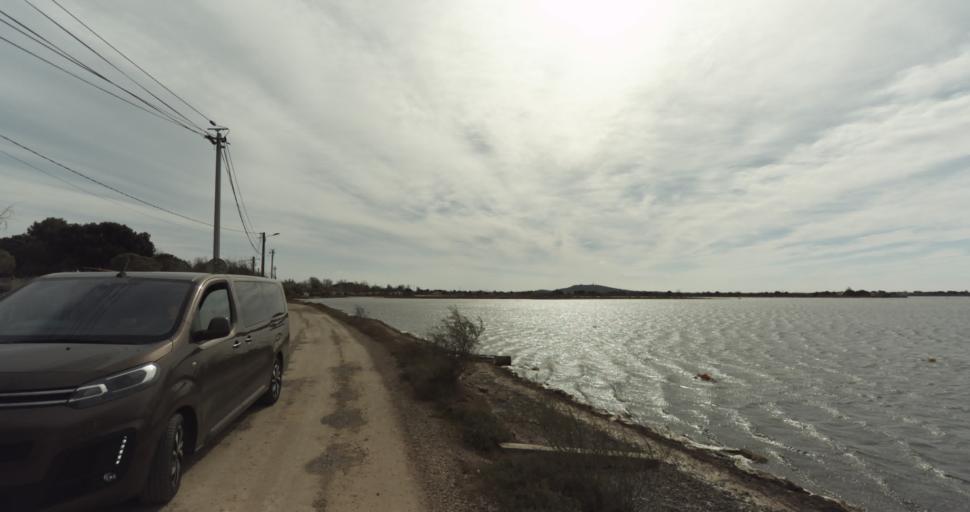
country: FR
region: Languedoc-Roussillon
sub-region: Departement de l'Herault
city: Marseillan
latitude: 43.3324
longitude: 3.5485
